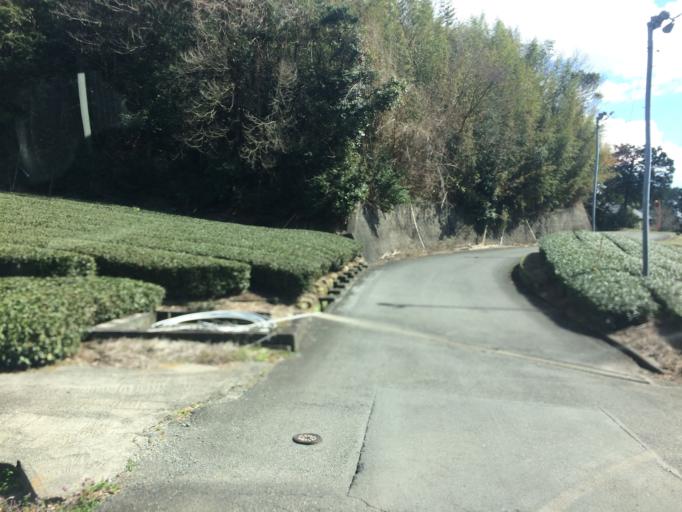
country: JP
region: Shizuoka
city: Shimada
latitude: 34.7672
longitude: 138.1962
